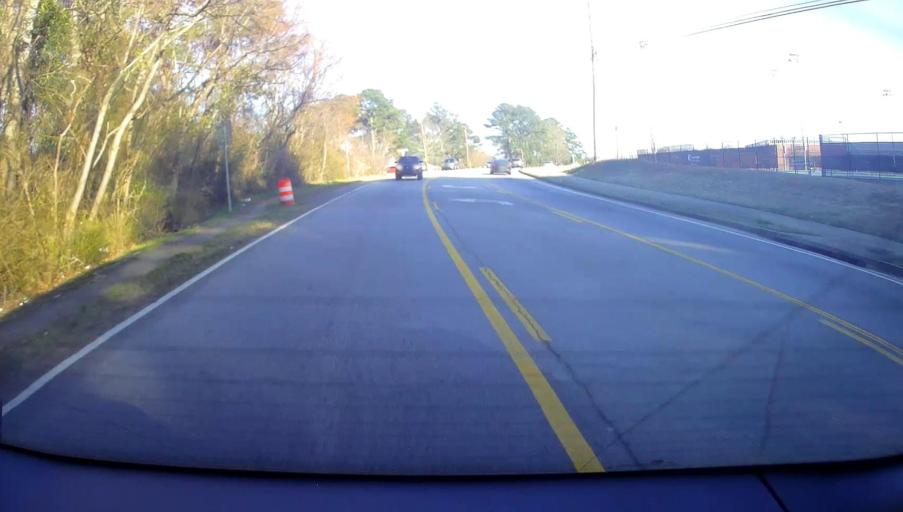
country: US
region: Georgia
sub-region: Clayton County
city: Bonanza
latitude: 33.4490
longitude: -84.3336
